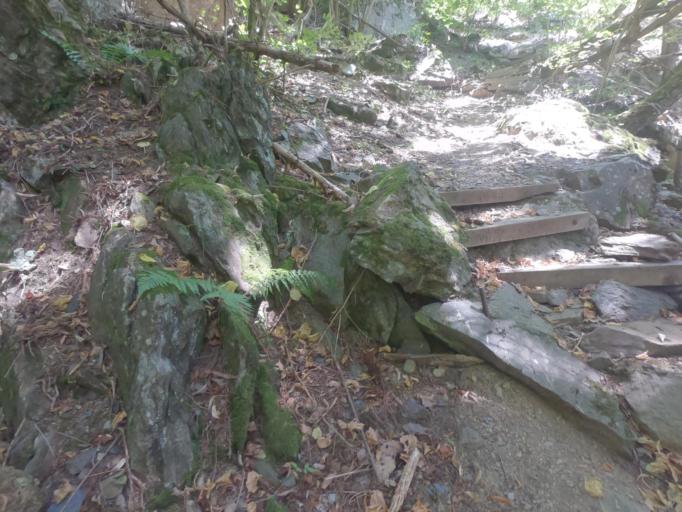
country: CH
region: Valais
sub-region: Saint-Maurice District
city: Salvan
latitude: 46.0796
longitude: 6.9766
